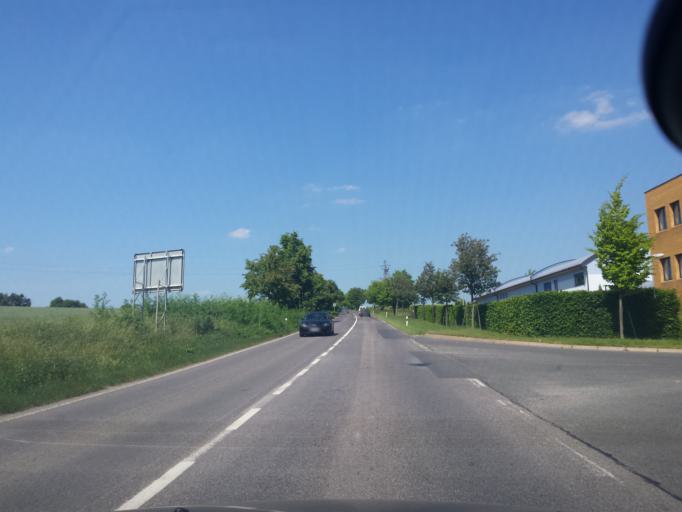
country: CZ
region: Central Bohemia
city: Velke Prilepy
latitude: 50.1650
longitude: 14.3135
